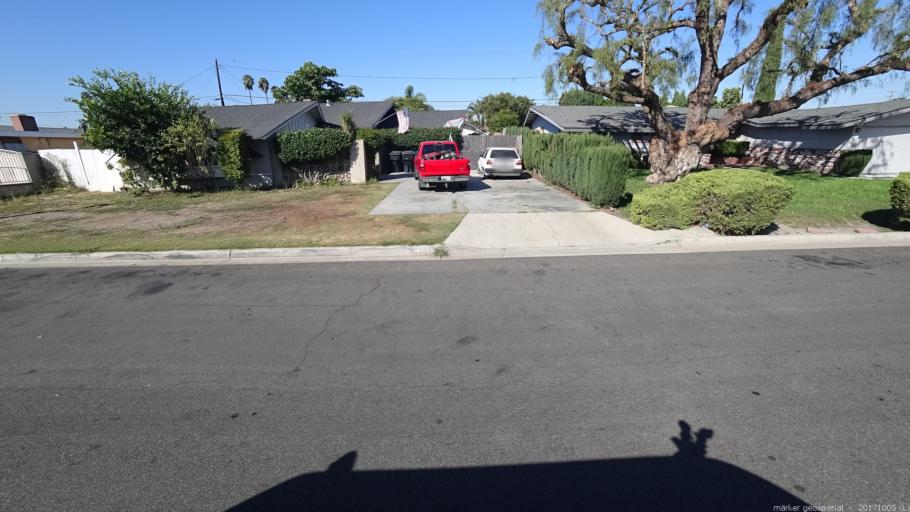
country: US
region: California
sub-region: Orange County
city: Garden Grove
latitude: 33.8015
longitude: -117.9544
